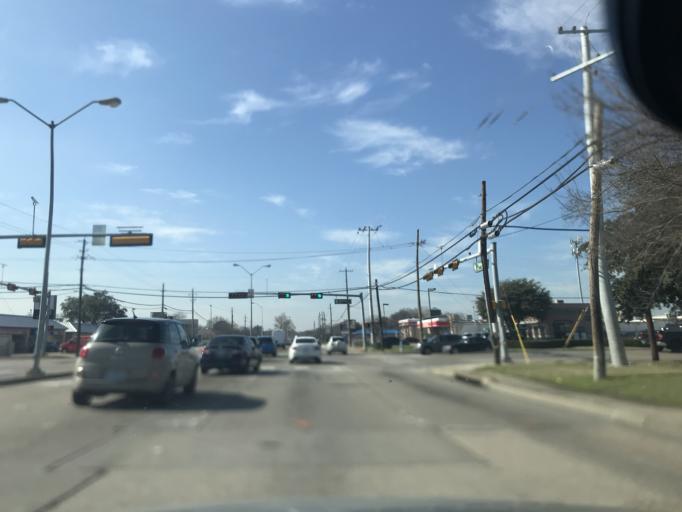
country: US
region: Texas
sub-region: Collin County
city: Plano
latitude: 33.0411
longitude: -96.7157
